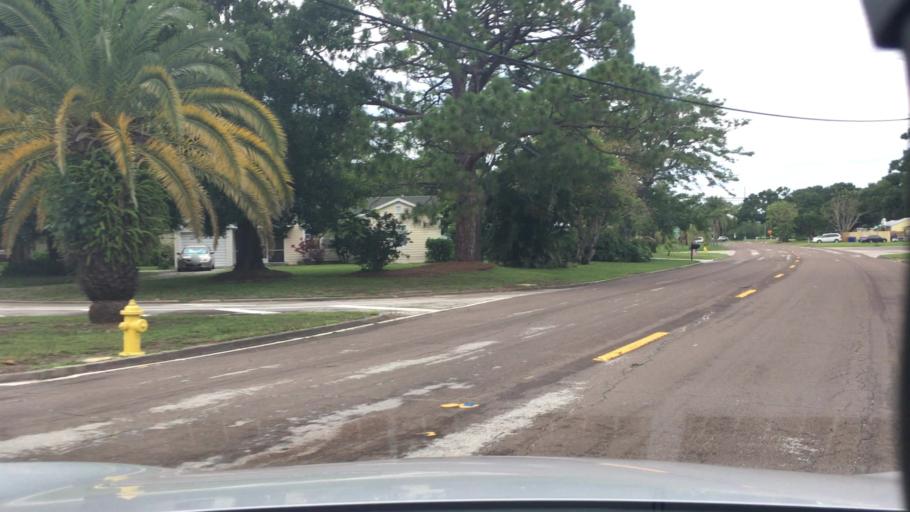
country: US
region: Florida
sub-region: Indian River County
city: Vero Beach
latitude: 27.6435
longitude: -80.4085
